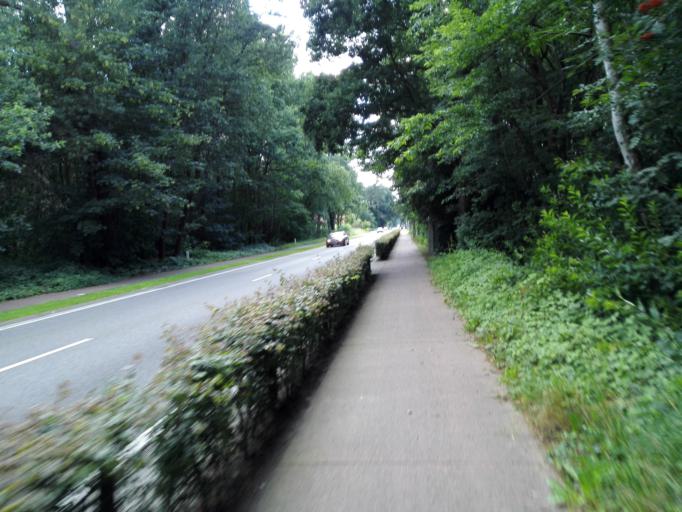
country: BE
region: Flanders
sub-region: Provincie Vlaams-Brabant
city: Boortmeerbeek
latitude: 51.0115
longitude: 4.5931
